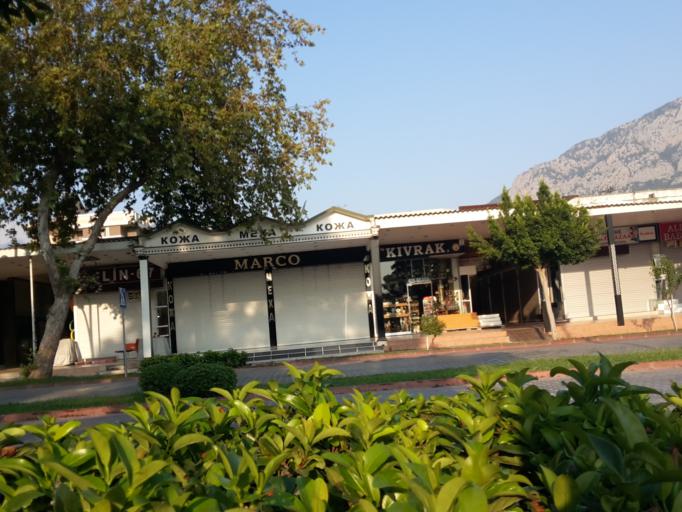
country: TR
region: Antalya
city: Kemer
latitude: 36.6041
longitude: 30.5594
